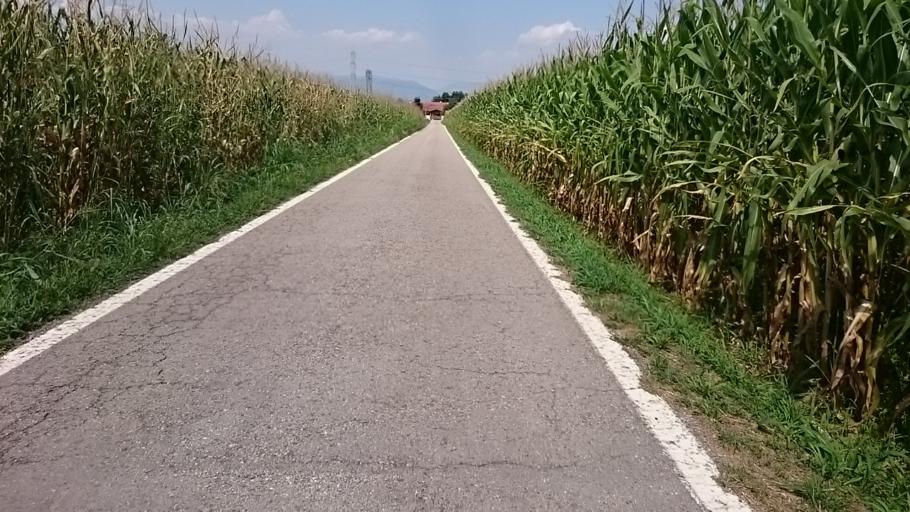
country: IT
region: Veneto
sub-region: Provincia di Padova
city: Fontaniva
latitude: 45.6655
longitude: 11.7495
